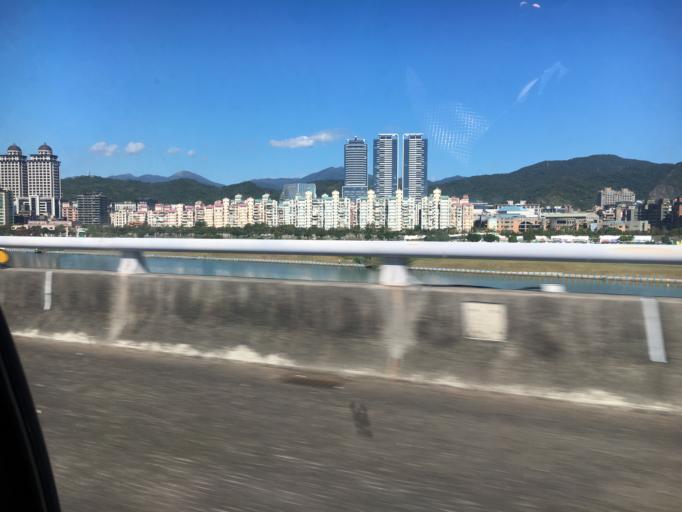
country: TW
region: Taipei
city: Taipei
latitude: 25.0723
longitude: 121.5592
